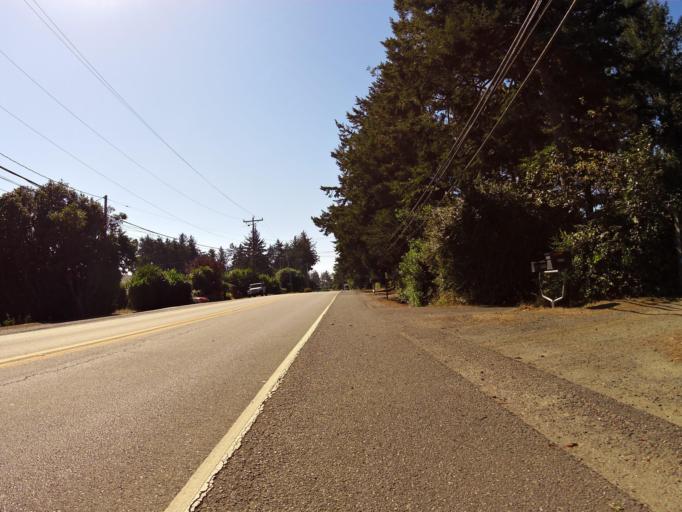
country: US
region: Oregon
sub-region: Coos County
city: Barview
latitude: 43.3543
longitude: -124.3121
